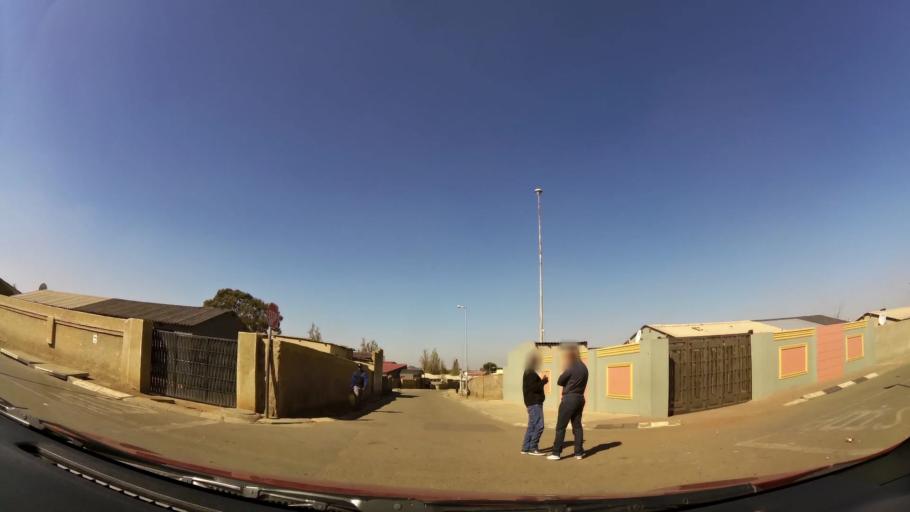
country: ZA
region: Gauteng
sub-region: City of Johannesburg Metropolitan Municipality
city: Soweto
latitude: -26.2381
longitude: 27.8421
